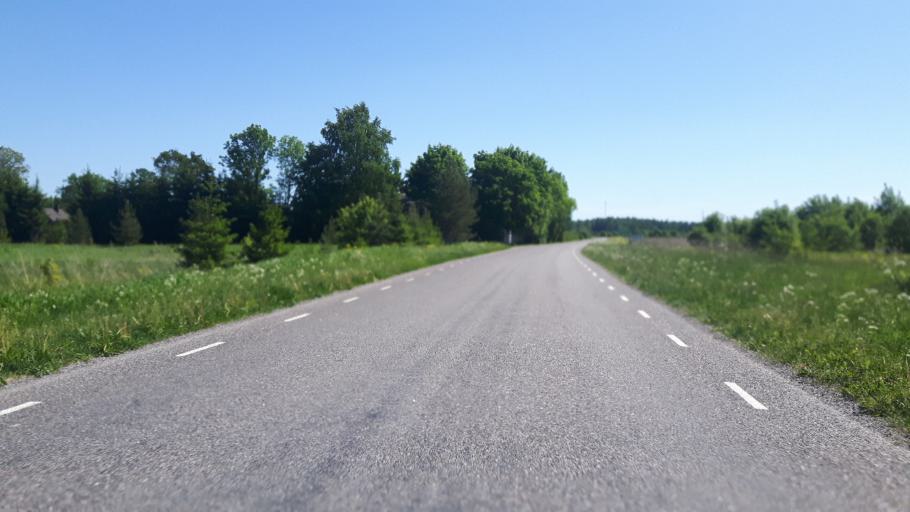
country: EE
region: Raplamaa
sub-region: Kohila vald
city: Kohila
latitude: 59.1887
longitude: 24.7105
